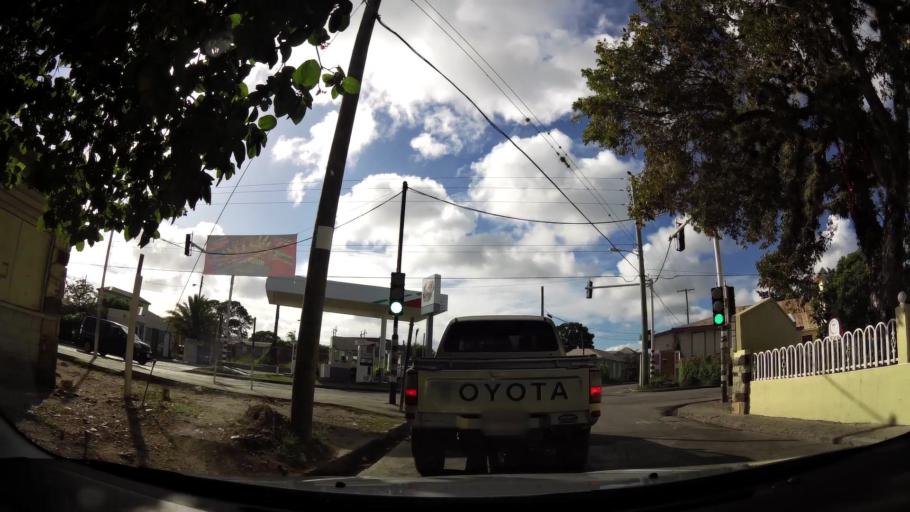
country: AG
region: Saint Peter
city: All Saints
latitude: 17.0641
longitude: -61.7945
